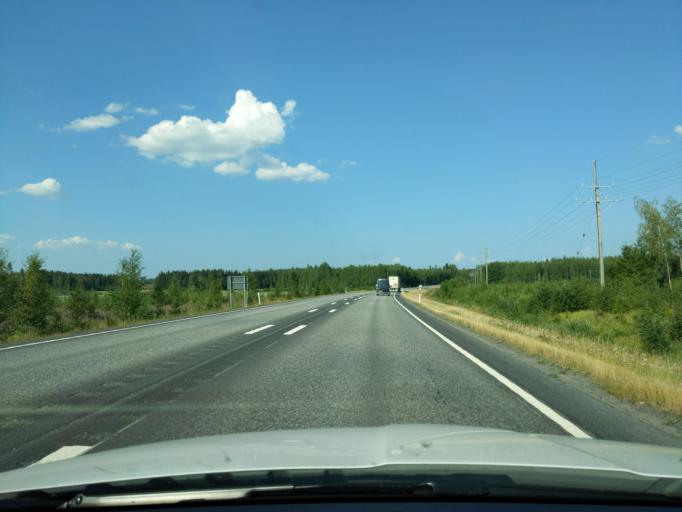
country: FI
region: Paijanne Tavastia
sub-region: Lahti
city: Jaervelae
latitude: 60.9213
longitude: 25.3598
